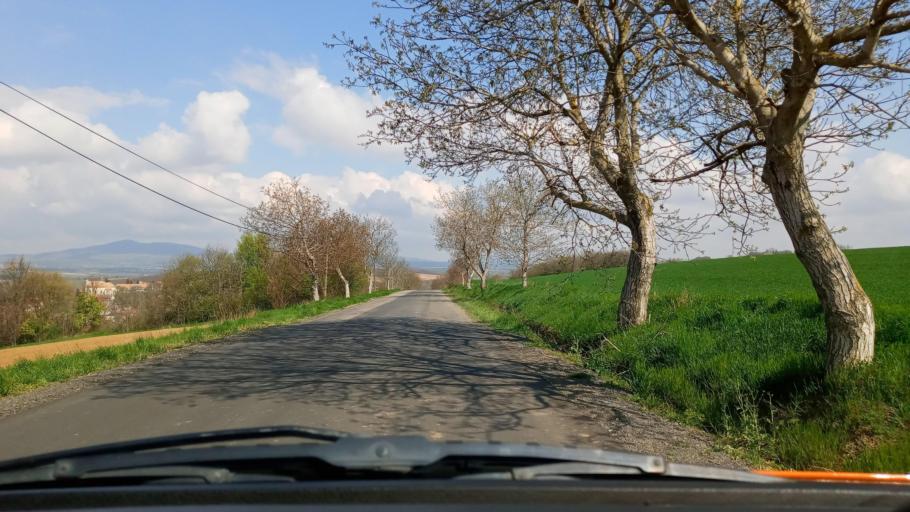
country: HU
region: Baranya
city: Pecsvarad
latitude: 46.0953
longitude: 18.4635
